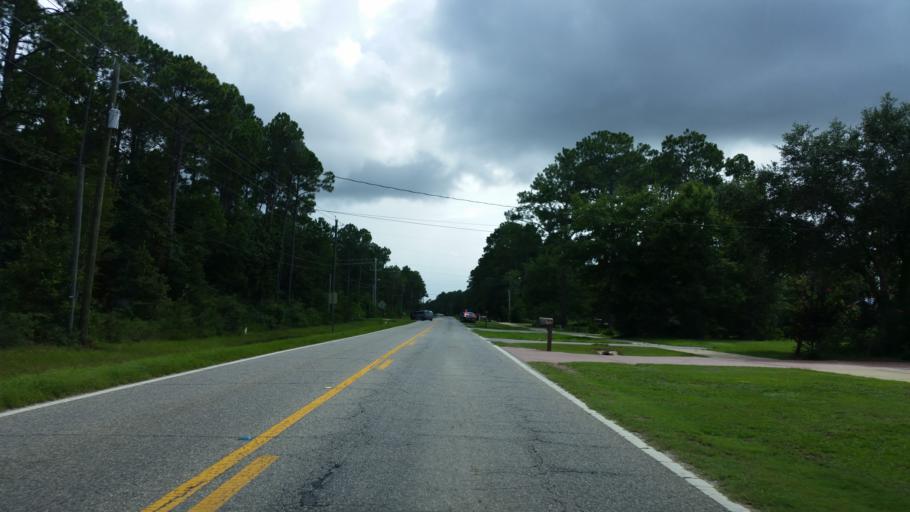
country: US
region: Florida
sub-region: Santa Rosa County
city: Holley
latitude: 30.4451
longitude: -86.9469
